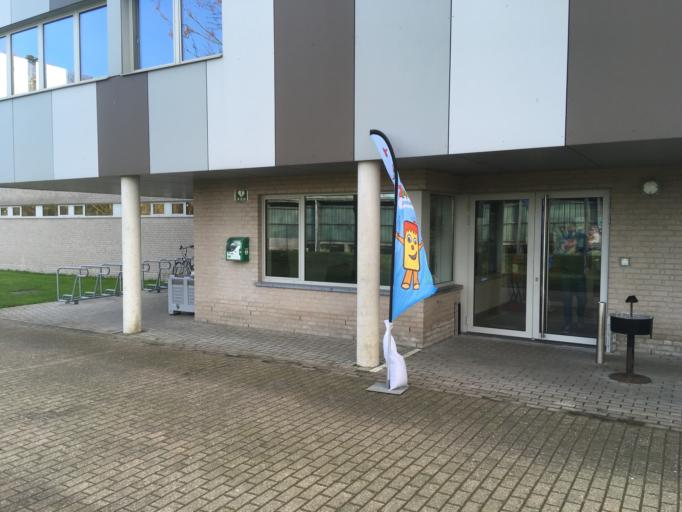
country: BE
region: Flanders
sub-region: Provincie West-Vlaanderen
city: Roeselare
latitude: 50.9668
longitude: 3.1434
